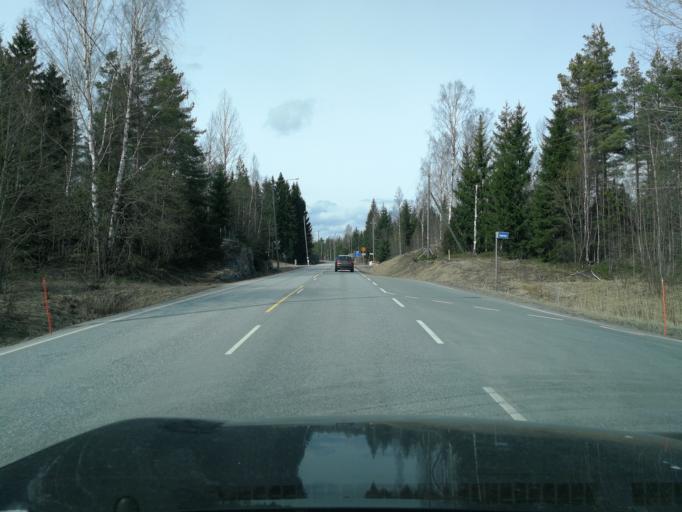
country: FI
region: Uusimaa
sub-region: Helsinki
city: Siuntio
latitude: 60.0963
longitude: 24.2519
